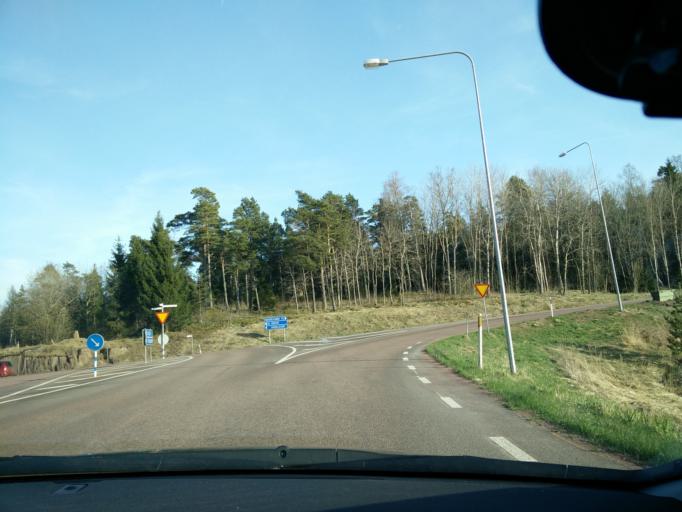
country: AX
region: Alands landsbygd
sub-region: Finstroem
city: Finstroem
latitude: 60.2288
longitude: 19.9898
